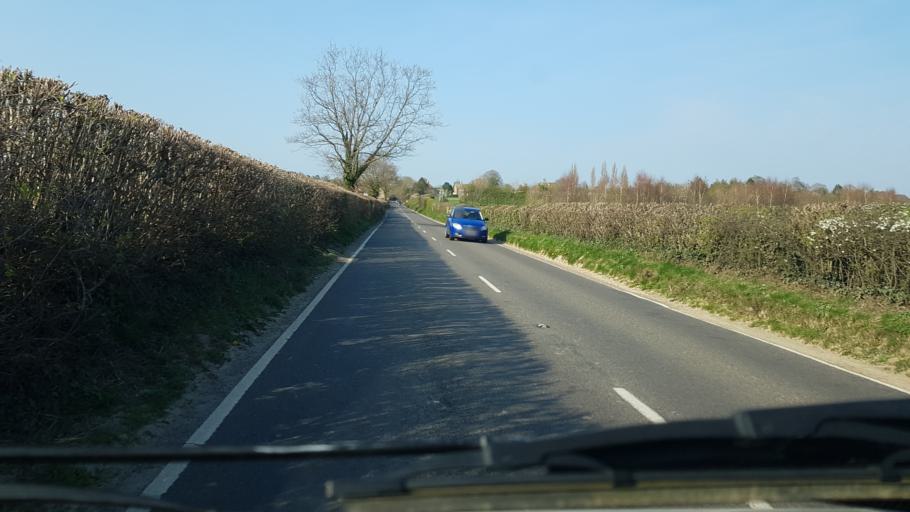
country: GB
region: England
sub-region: West Sussex
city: Petworth
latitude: 50.9768
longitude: -0.6131
